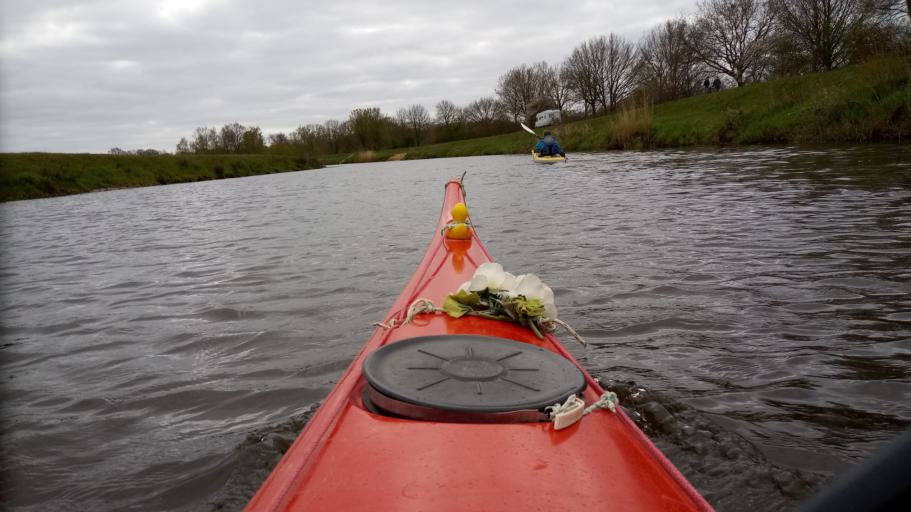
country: NL
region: Overijssel
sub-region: Gemeente Twenterand
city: Den Ham
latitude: 52.4931
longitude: 6.4173
